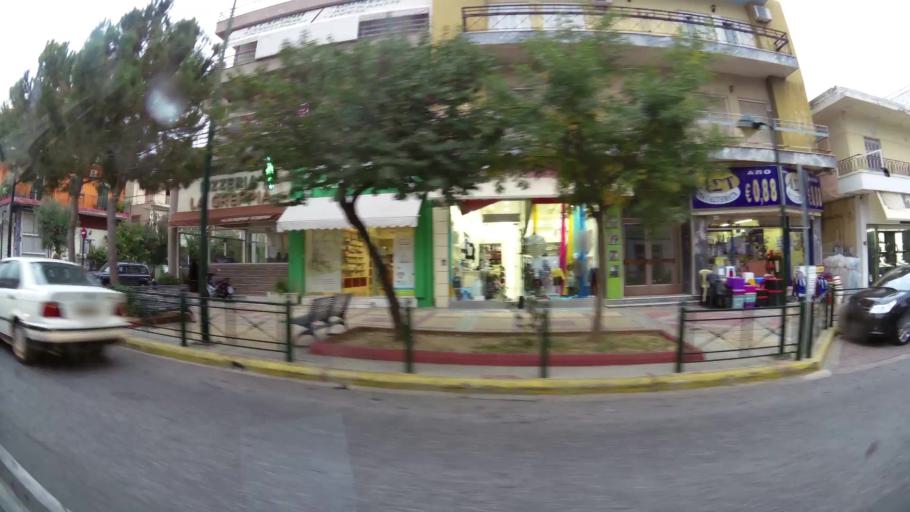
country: GR
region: Attica
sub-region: Nomarchia Athinas
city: Agia Varvara
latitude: 37.9885
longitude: 23.6591
